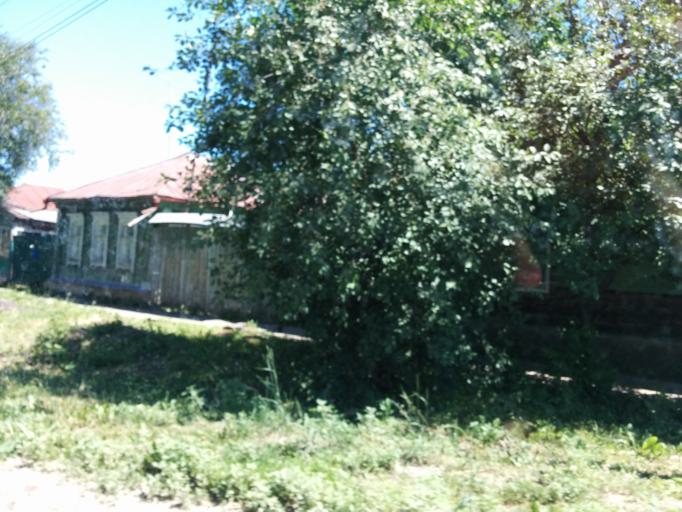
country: RU
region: Tambov
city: Morshansk
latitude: 53.4408
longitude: 41.7990
